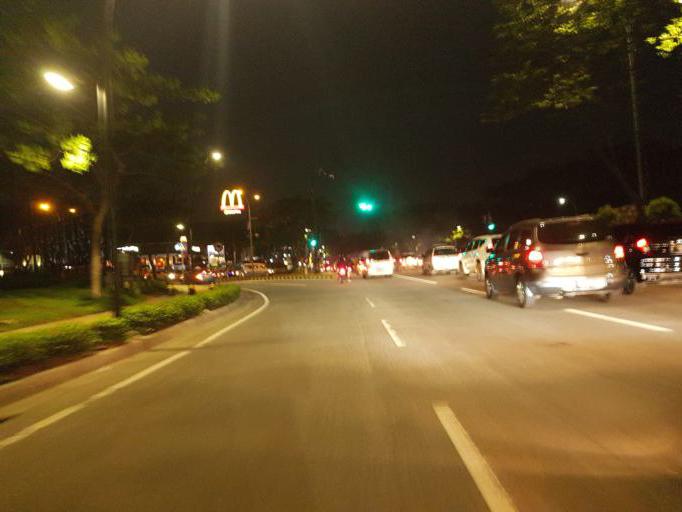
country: ID
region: West Java
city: Serpong
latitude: -6.2997
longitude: 106.6633
